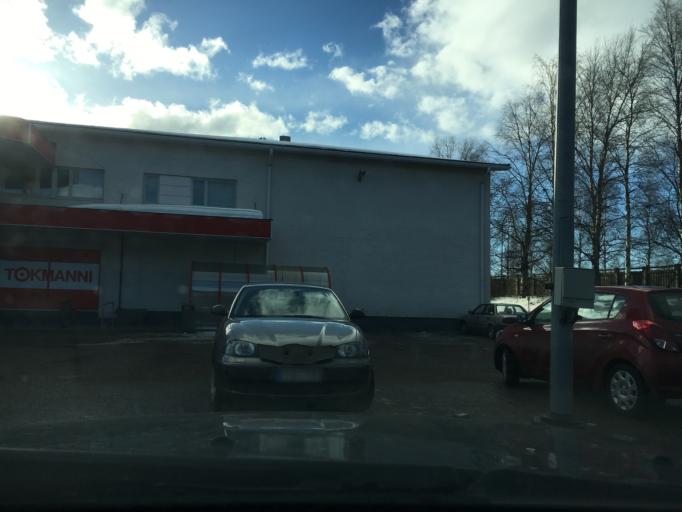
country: FI
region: Kainuu
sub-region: Kajaani
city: Kajaani
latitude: 64.2187
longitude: 27.7437
